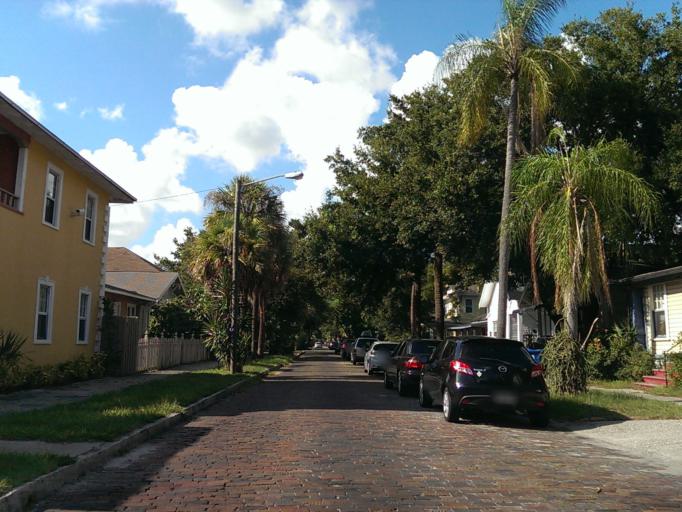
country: US
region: Florida
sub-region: Pinellas County
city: Saint Petersburg
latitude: 27.7777
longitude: -82.6406
